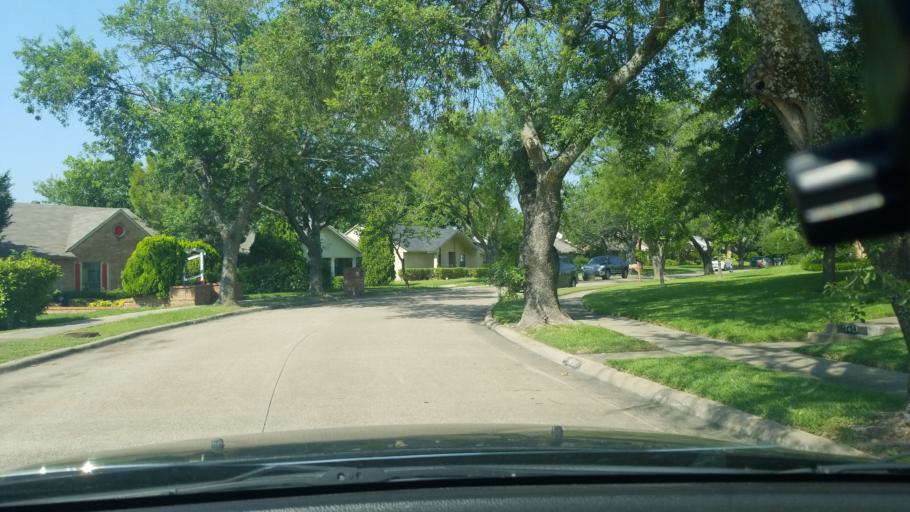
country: US
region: Texas
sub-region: Dallas County
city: Mesquite
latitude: 32.8213
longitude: -96.6217
